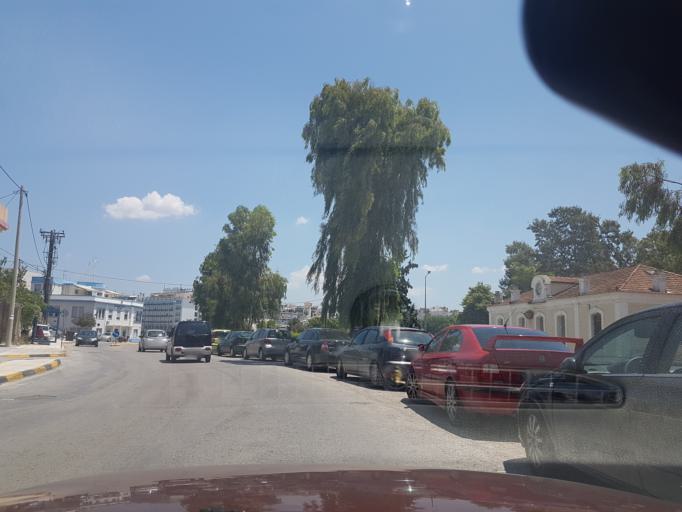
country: GR
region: Central Greece
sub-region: Nomos Evvoias
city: Chalkida
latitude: 38.4629
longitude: 23.5874
